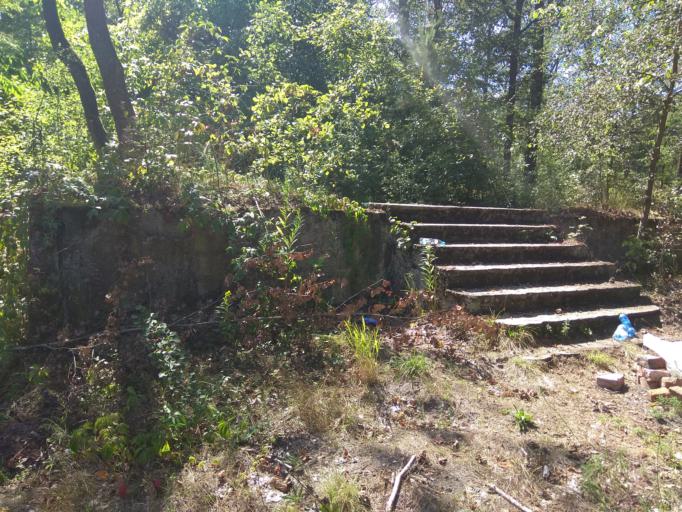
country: PL
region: Lower Silesian Voivodeship
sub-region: Powiat sredzki
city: Mrozow
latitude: 51.1787
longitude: 16.8539
